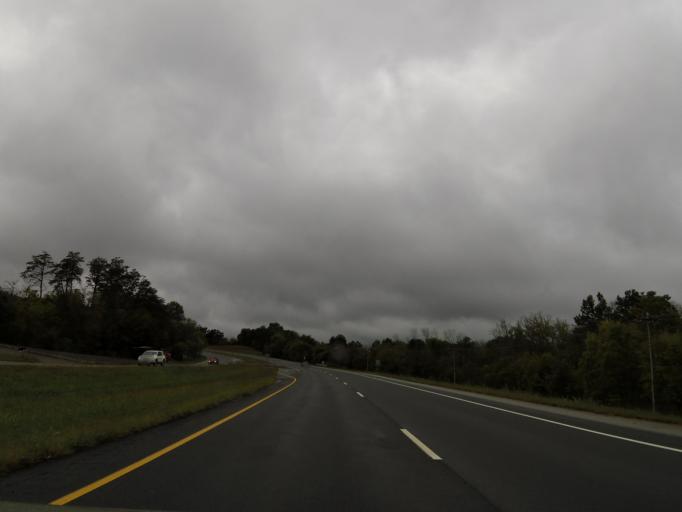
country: US
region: Tennessee
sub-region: Loudon County
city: Greenback
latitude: 35.7548
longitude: -84.1299
